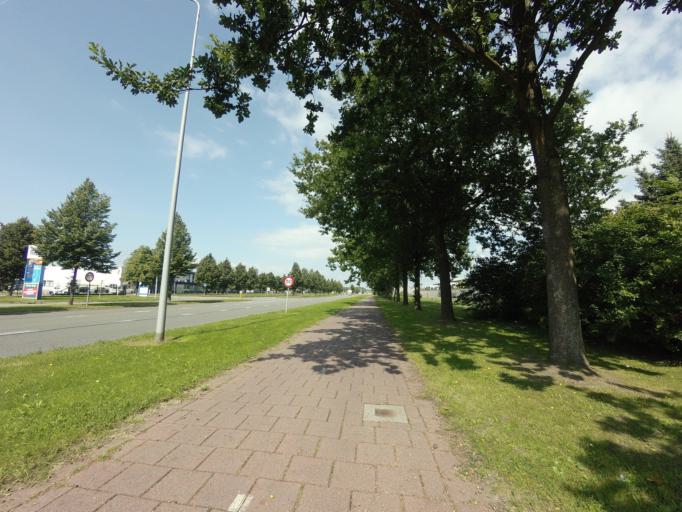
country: NL
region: Flevoland
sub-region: Gemeente Lelystad
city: Lelystad
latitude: 52.5318
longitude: 5.5196
